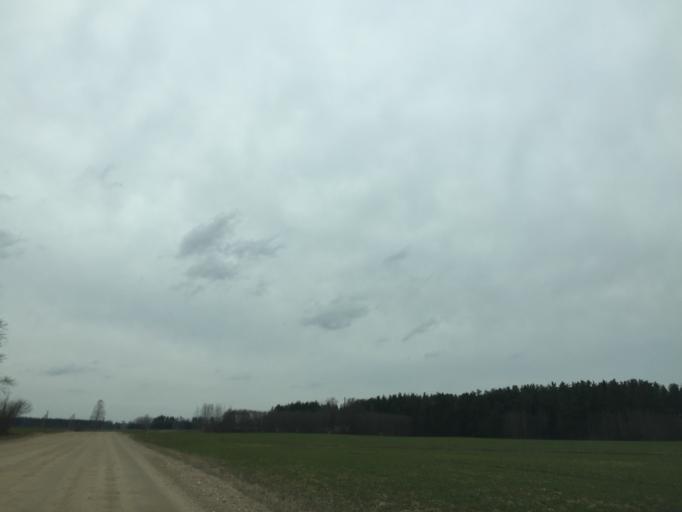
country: LV
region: Livani
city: Livani
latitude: 56.3111
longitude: 26.1629
